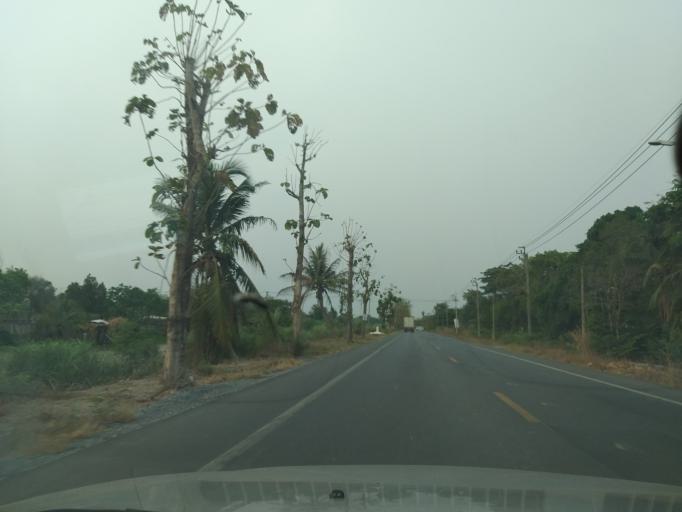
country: TH
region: Bangkok
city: Nong Chok
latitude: 13.9330
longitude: 100.8936
